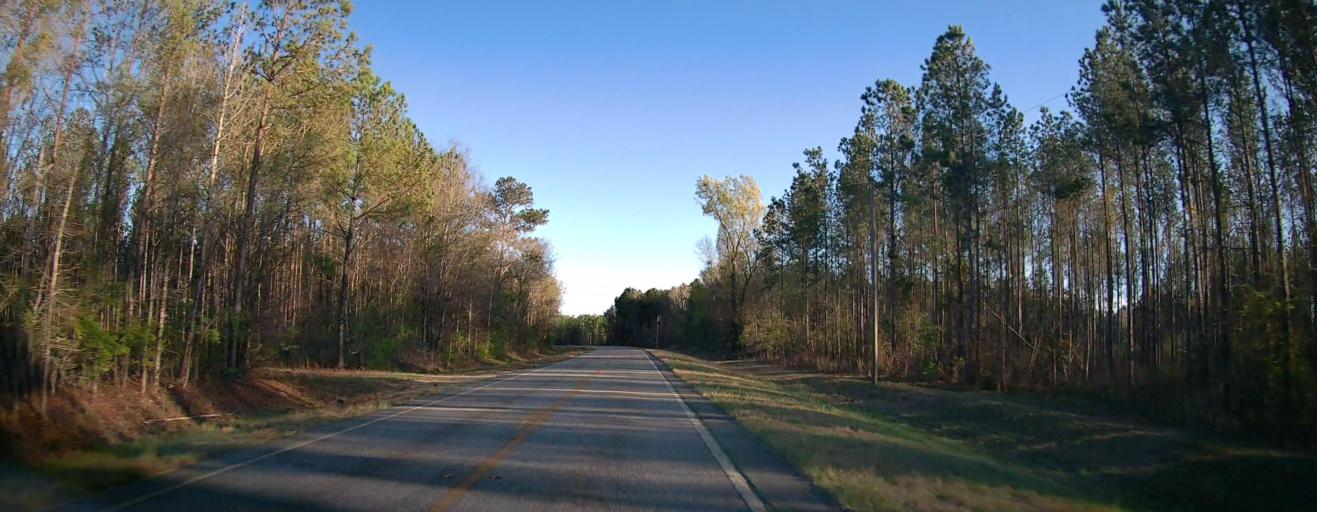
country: US
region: Georgia
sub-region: Wilcox County
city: Abbeville
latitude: 32.0724
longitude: -83.2838
